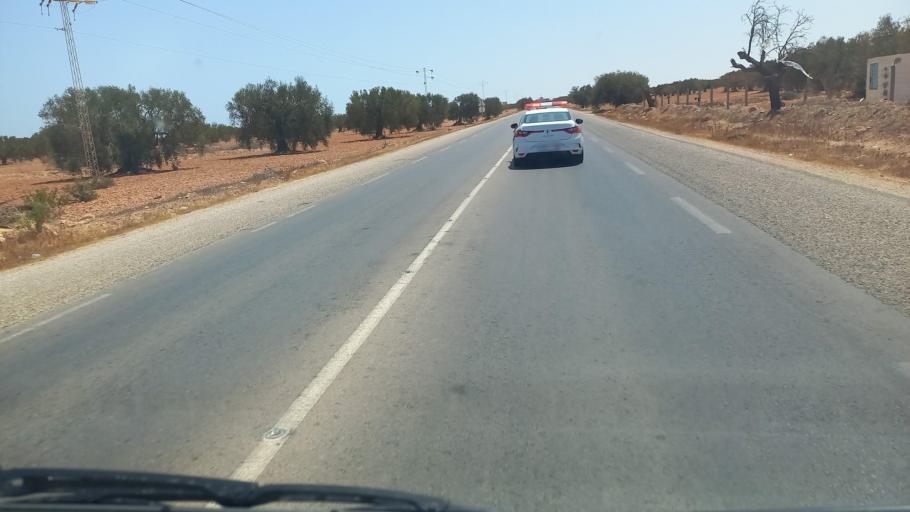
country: TN
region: Madanin
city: Zarzis
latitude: 33.5571
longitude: 11.0591
